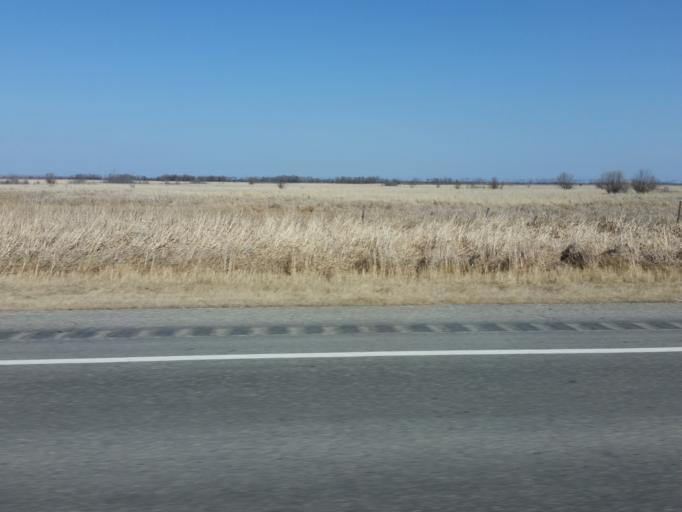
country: US
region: North Dakota
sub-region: Grand Forks County
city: Grand Forks Air Force Base
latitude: 48.1456
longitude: -97.2637
